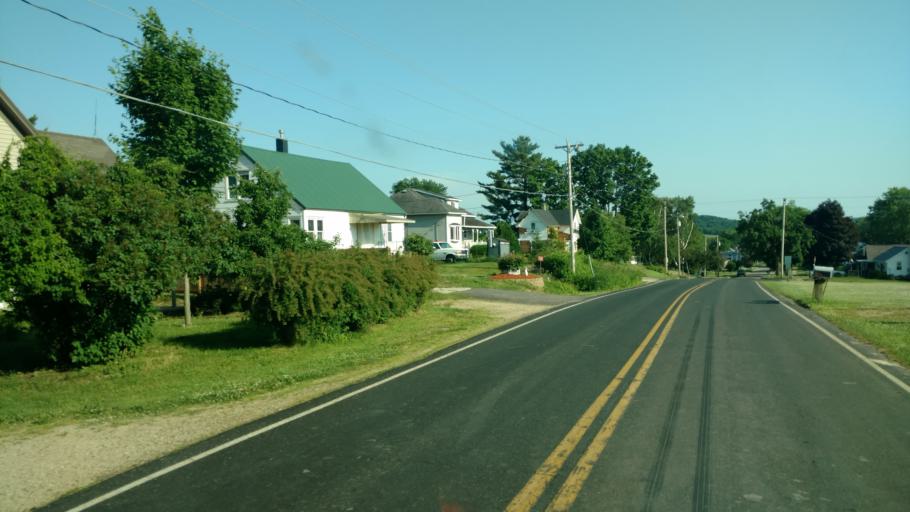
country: US
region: Wisconsin
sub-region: Vernon County
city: Hillsboro
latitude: 43.6593
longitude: -90.3459
